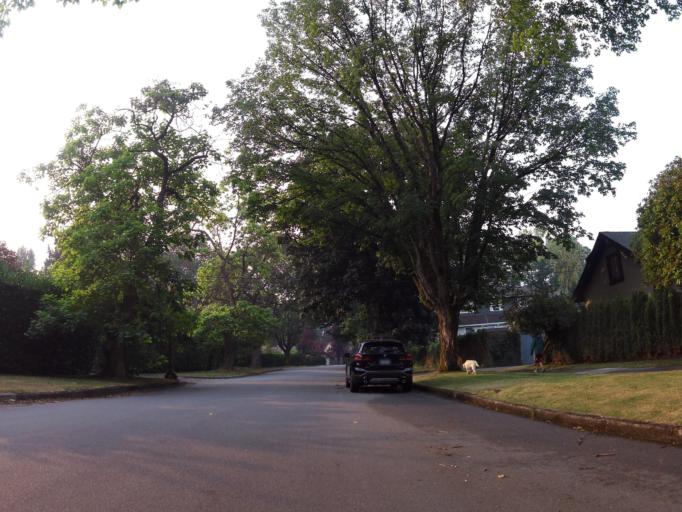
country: CA
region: British Columbia
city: Vancouver
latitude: 49.2398
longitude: -123.1456
